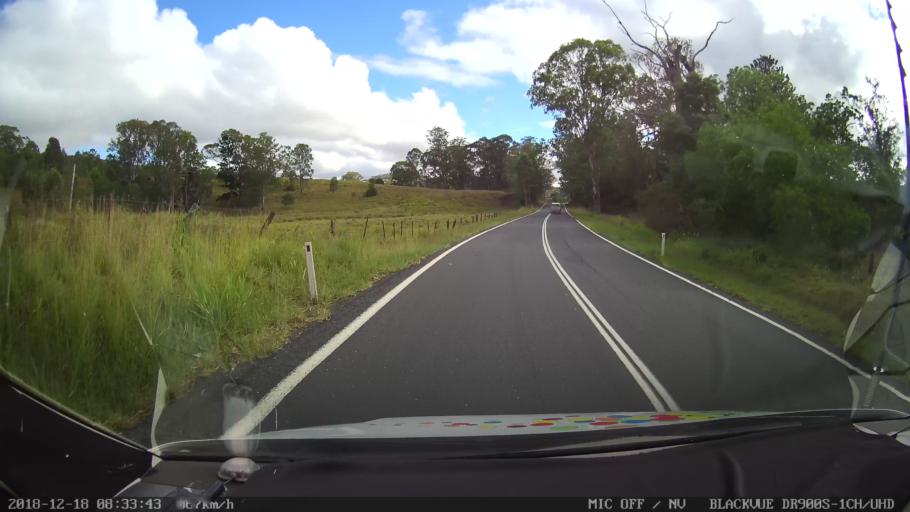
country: AU
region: New South Wales
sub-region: Kyogle
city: Kyogle
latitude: -28.2885
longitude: 152.7862
